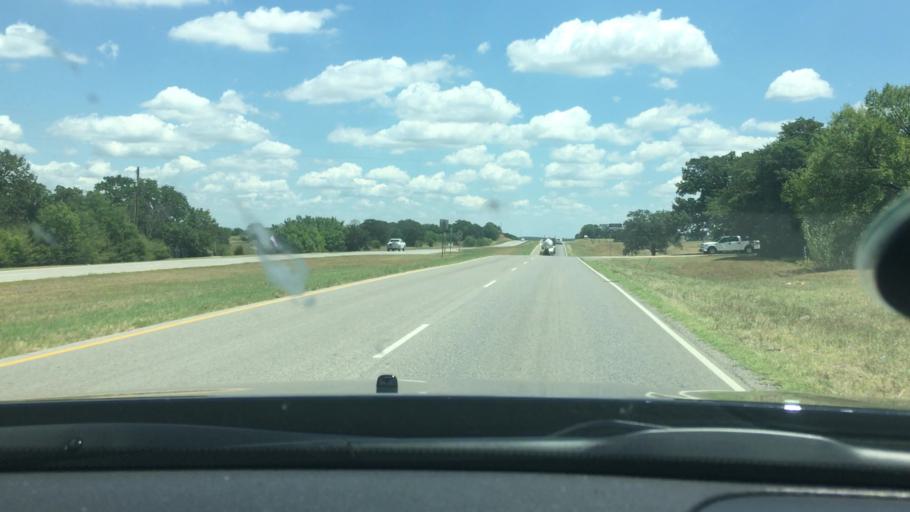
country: US
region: Oklahoma
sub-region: Carter County
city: Wilson
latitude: 34.1728
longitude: -97.3947
